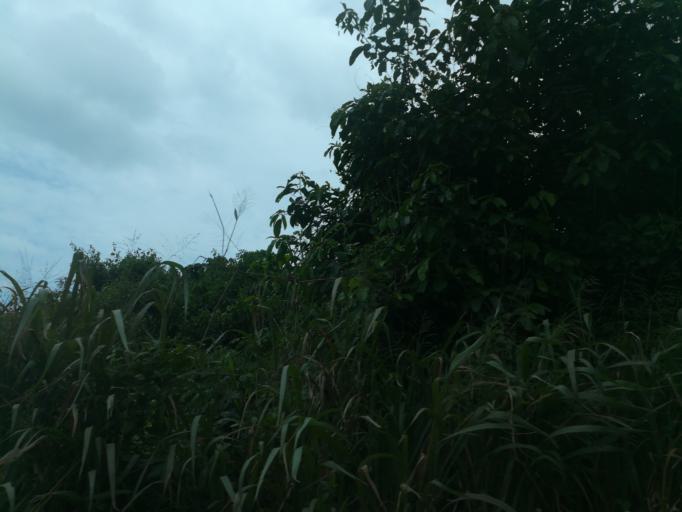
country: NG
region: Lagos
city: Ejirin
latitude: 6.6436
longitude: 3.8536
